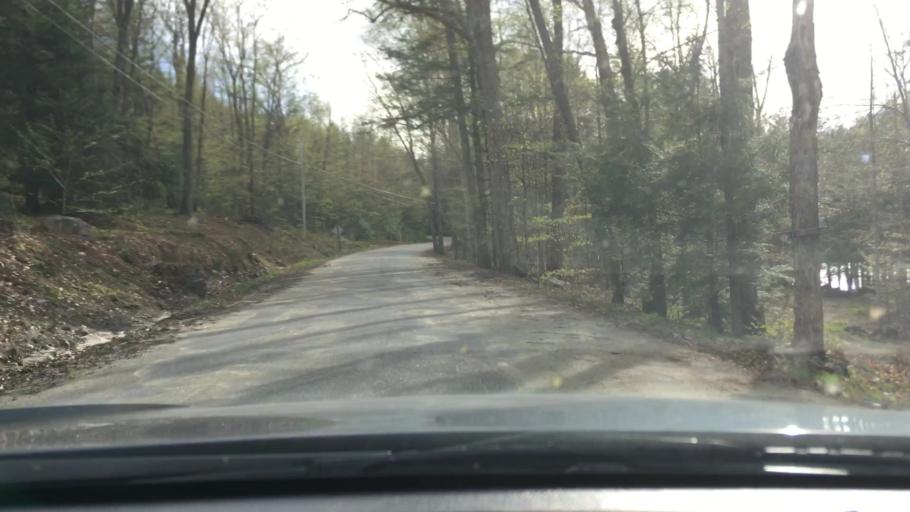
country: US
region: New York
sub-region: Essex County
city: Ticonderoga
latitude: 43.8177
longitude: -73.7420
